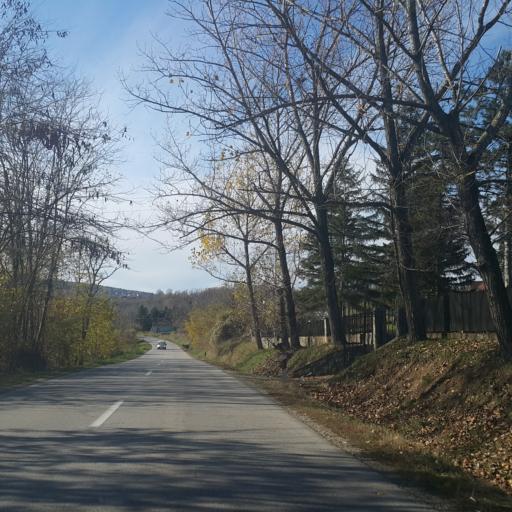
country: RS
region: Central Serbia
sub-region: Sumadijski Okrug
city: Topola
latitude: 44.2499
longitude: 20.7203
